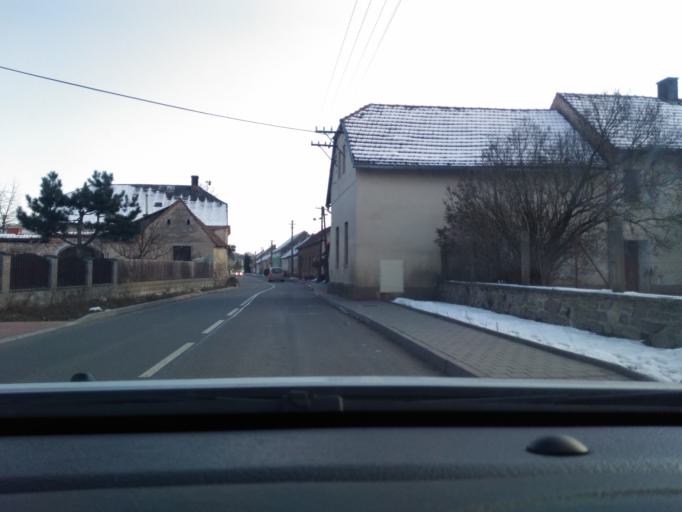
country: CZ
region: South Moravian
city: Predklasteri
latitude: 49.3744
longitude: 16.3861
